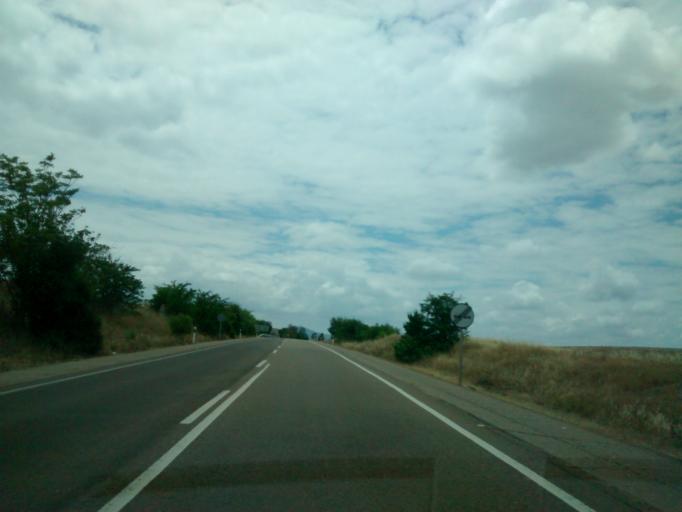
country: ES
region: Extremadura
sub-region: Provincia de Badajoz
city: Merida
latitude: 38.9323
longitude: -6.3121
